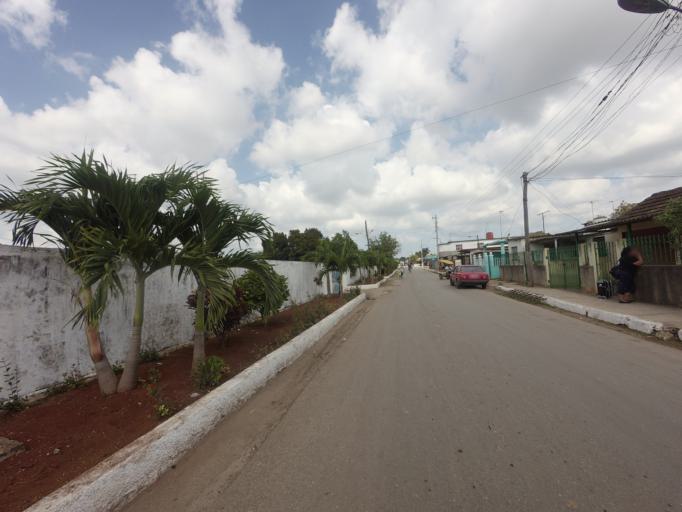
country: CU
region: Artemisa
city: Bauta
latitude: 22.9824
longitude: -82.5511
